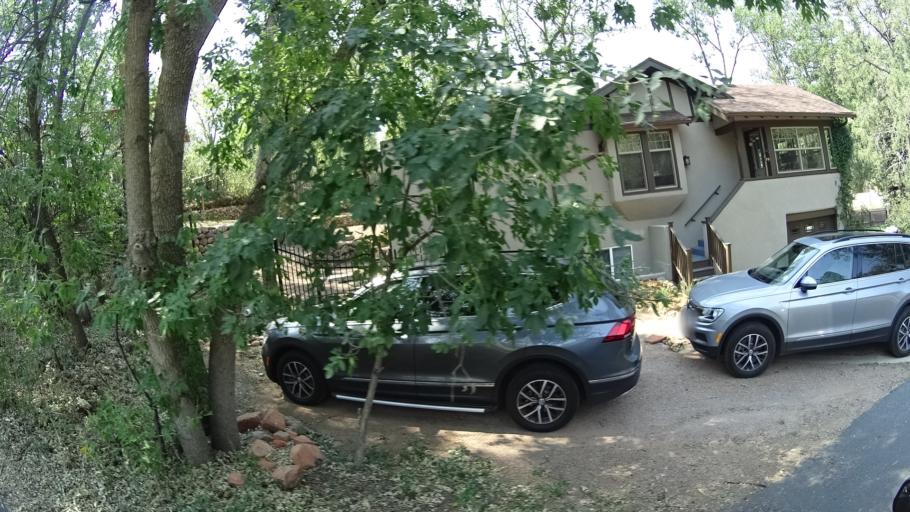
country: US
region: Colorado
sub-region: El Paso County
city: Colorado Springs
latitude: 38.7942
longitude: -104.8534
